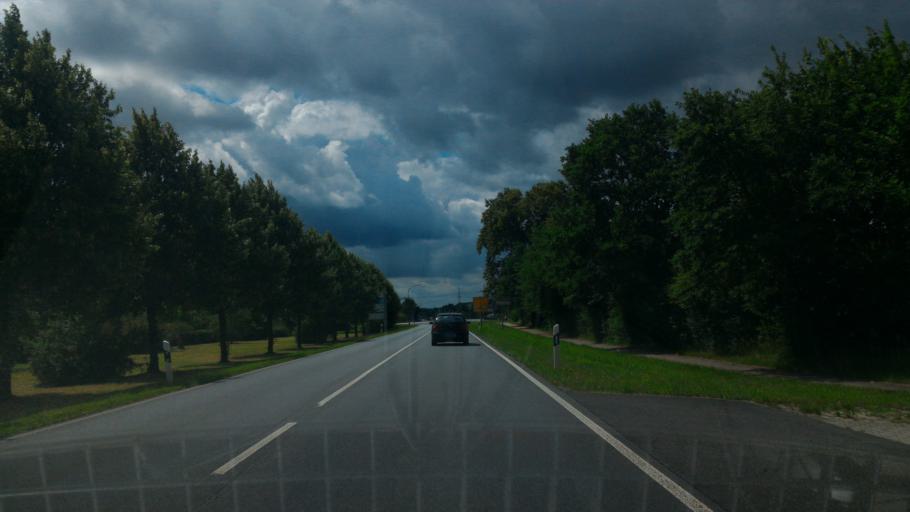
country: DE
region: Saxony
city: Ostritz
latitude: 51.0678
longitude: 14.9598
